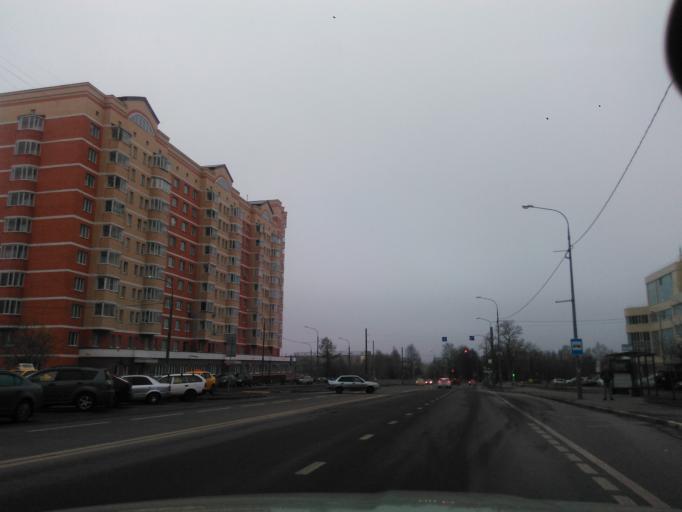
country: RU
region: Moscow
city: Zelenograd
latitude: 55.9719
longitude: 37.1620
